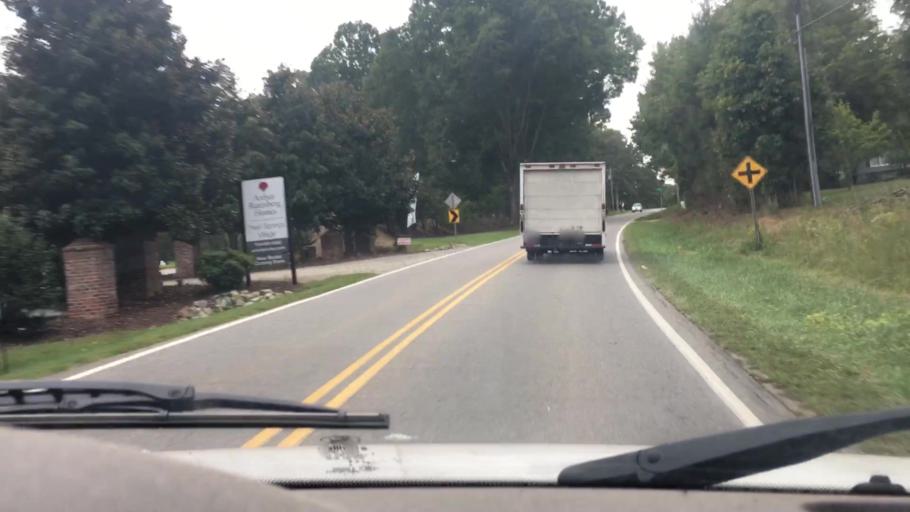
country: US
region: North Carolina
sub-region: Catawba County
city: Lake Norman of Catawba
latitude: 35.5566
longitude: -80.9908
